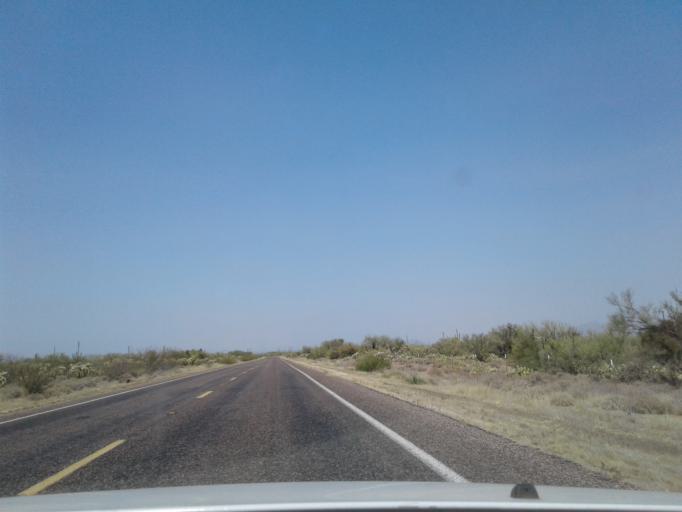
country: US
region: Arizona
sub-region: Pima County
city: Marana
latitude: 32.6379
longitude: -111.1395
